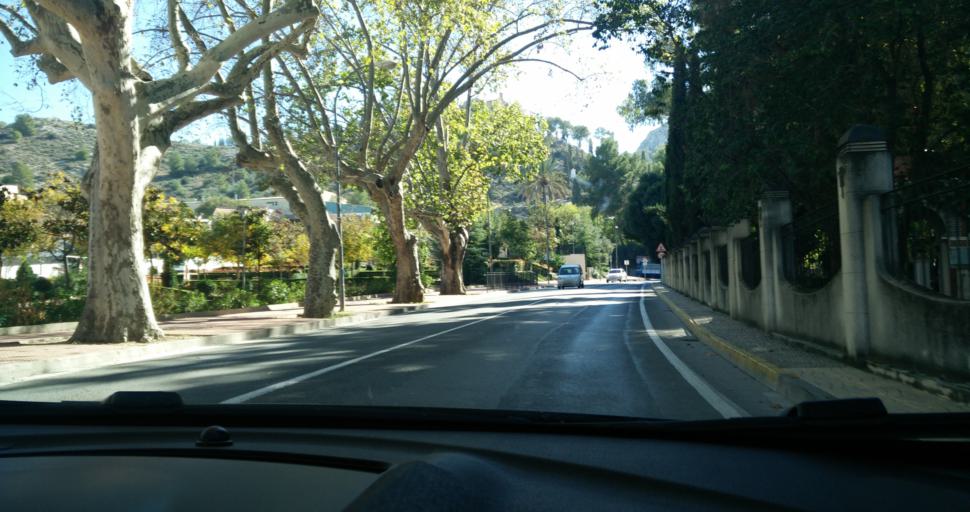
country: ES
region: Valencia
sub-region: Provincia de Valencia
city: Xativa
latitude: 38.9901
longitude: -0.5129
